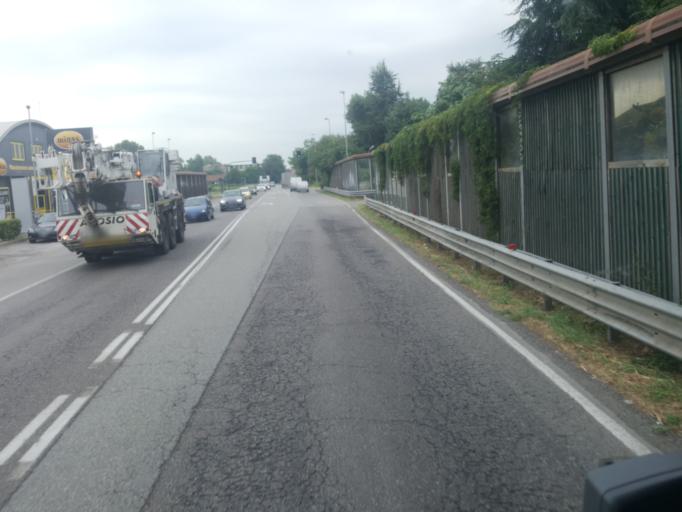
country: IT
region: Lombardy
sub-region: Citta metropolitana di Milano
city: Melzo
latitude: 45.4938
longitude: 9.4211
